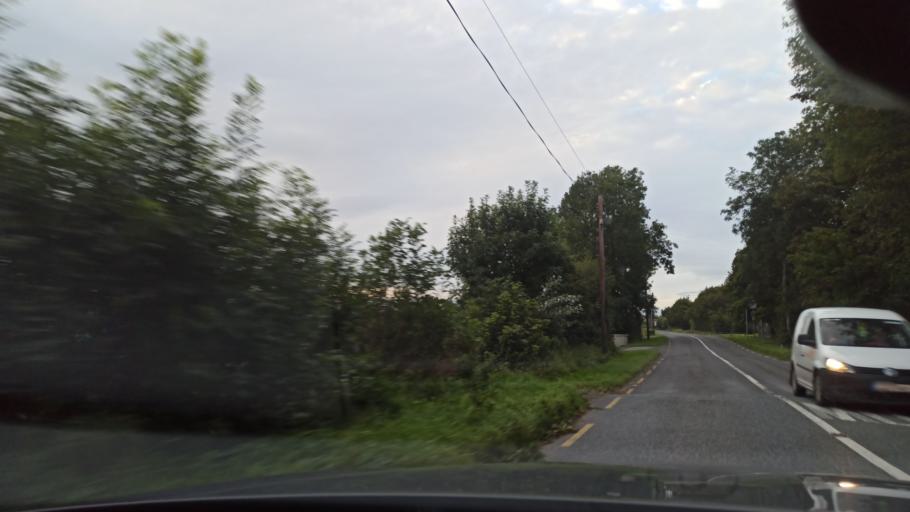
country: IE
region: Munster
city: Cashel
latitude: 52.4907
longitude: -7.8599
